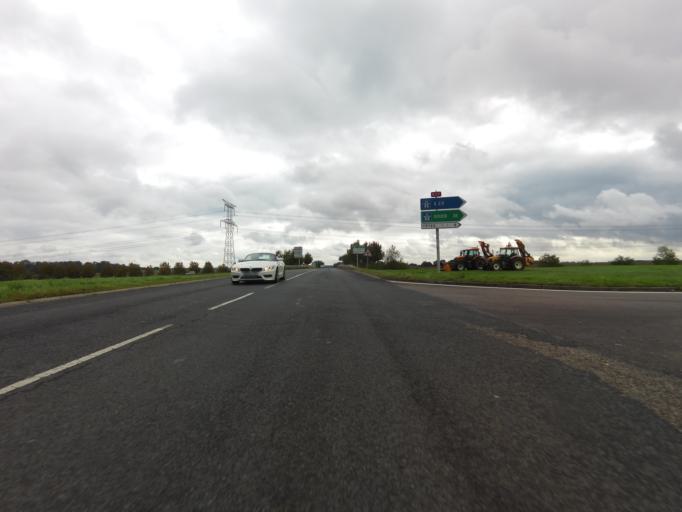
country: FR
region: Haute-Normandie
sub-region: Departement de la Seine-Maritime
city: Totes
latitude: 49.7189
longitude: 1.0599
